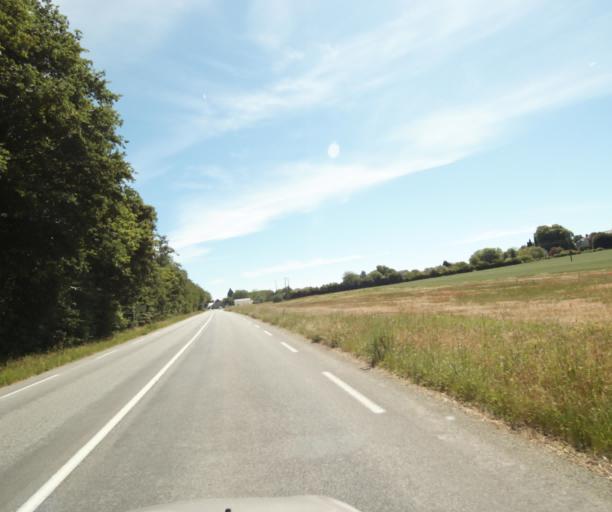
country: FR
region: Centre
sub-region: Departement d'Indre-et-Loire
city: Ligre
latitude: 47.1354
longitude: 0.2968
